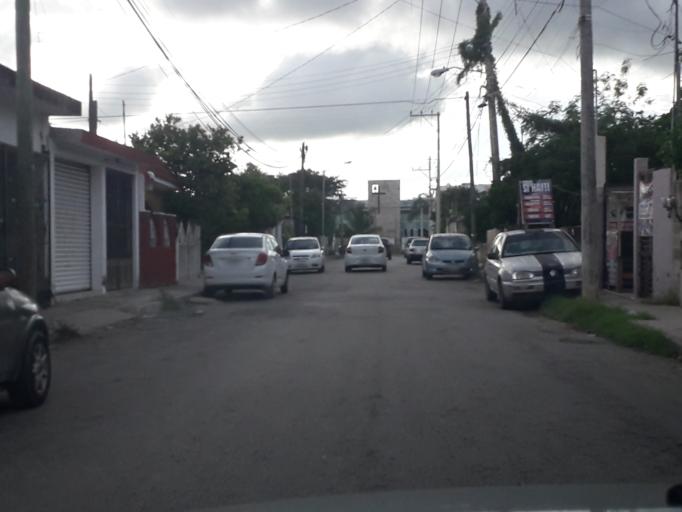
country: MX
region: Yucatan
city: Merida
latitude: 20.9617
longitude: -89.6544
